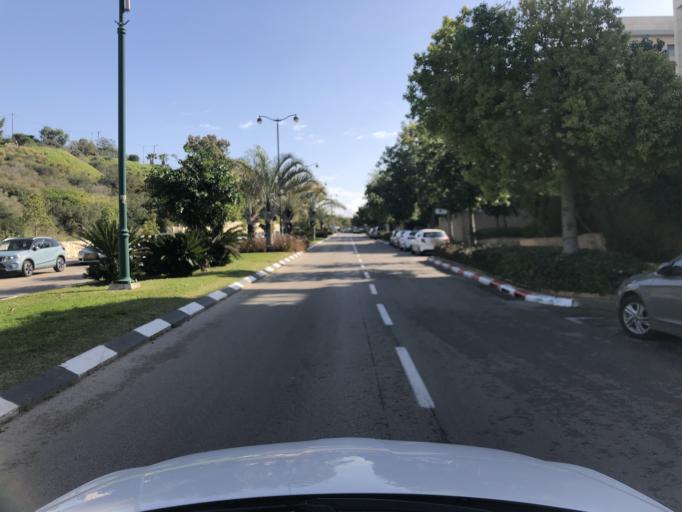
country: IL
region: Central District
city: Ness Ziona
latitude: 31.9146
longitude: 34.7899
